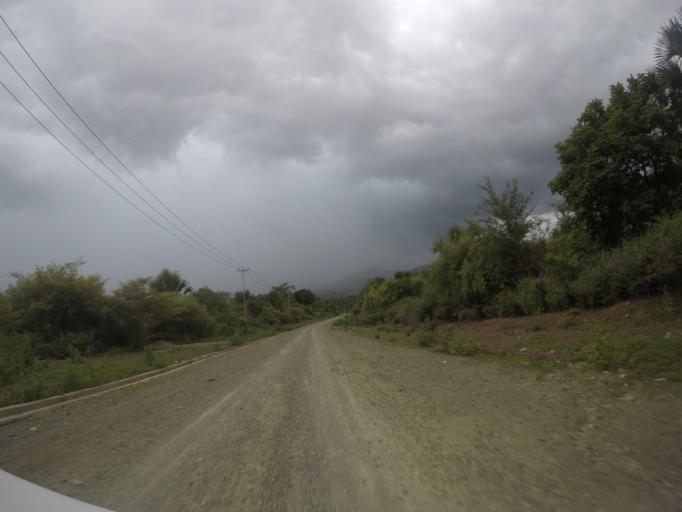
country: TL
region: Bobonaro
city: Maliana
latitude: -8.8502
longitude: 125.0753
